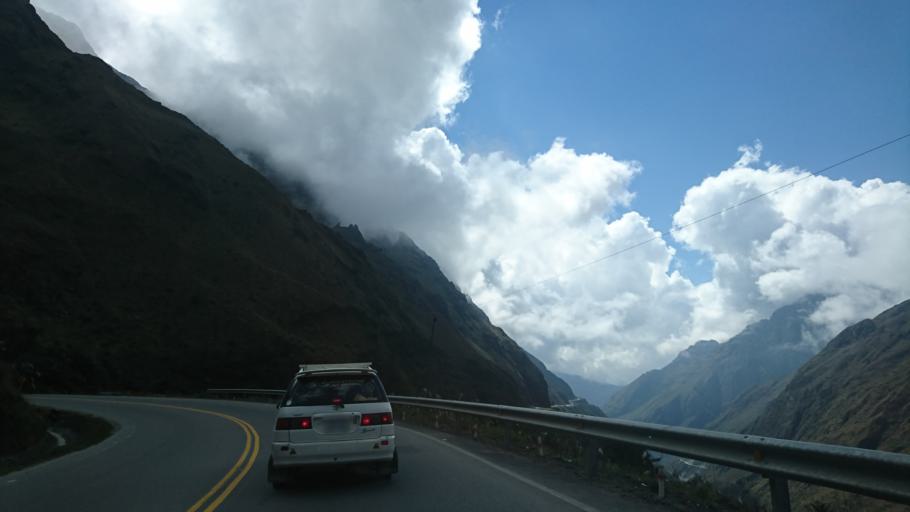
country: BO
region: La Paz
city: Coroico
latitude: -16.3164
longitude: -67.9261
